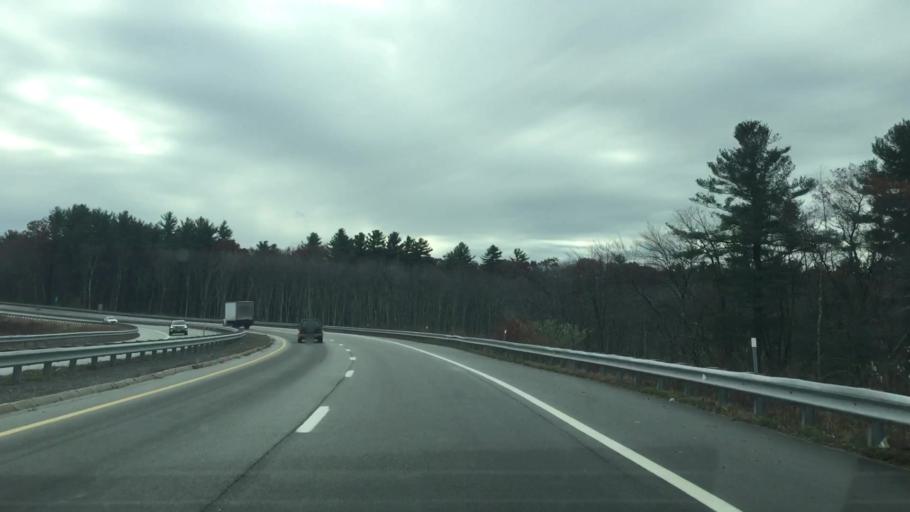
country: US
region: New Hampshire
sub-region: Rockingham County
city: Salem
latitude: 42.7598
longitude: -71.2341
